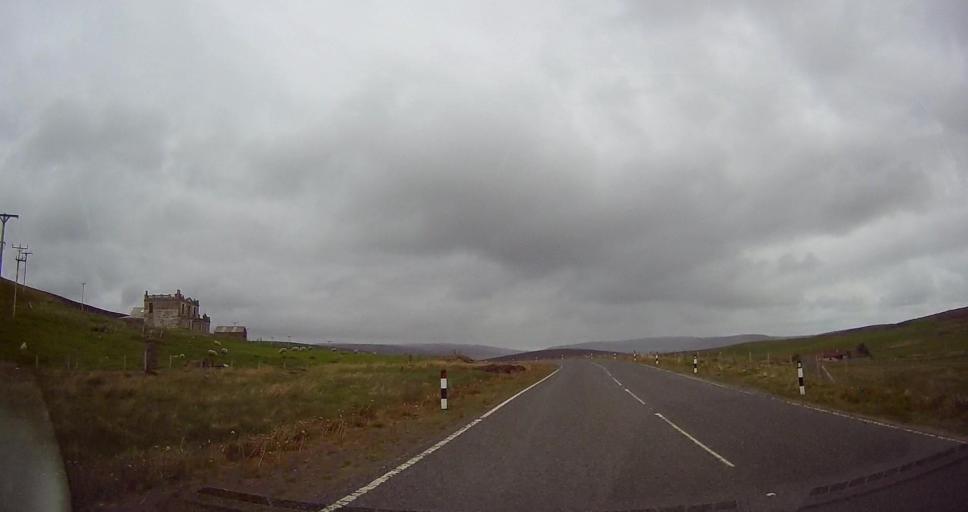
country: GB
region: Scotland
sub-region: Shetland Islands
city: Lerwick
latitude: 60.2571
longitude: -1.4398
